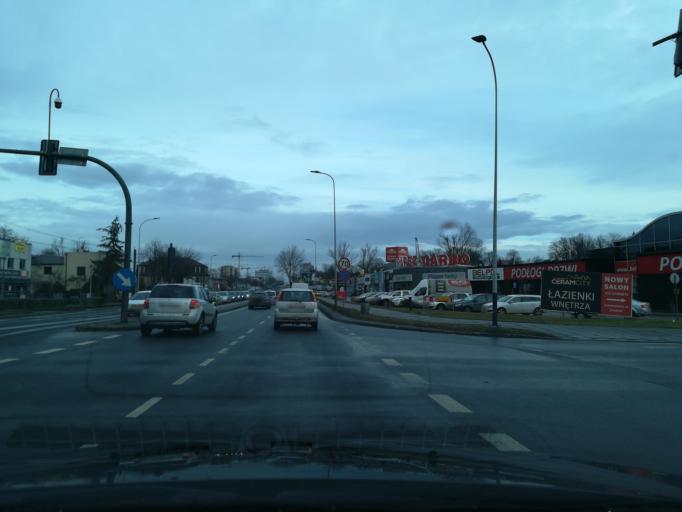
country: PL
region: Lesser Poland Voivodeship
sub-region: Krakow
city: Krakow
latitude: 50.0184
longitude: 19.9310
